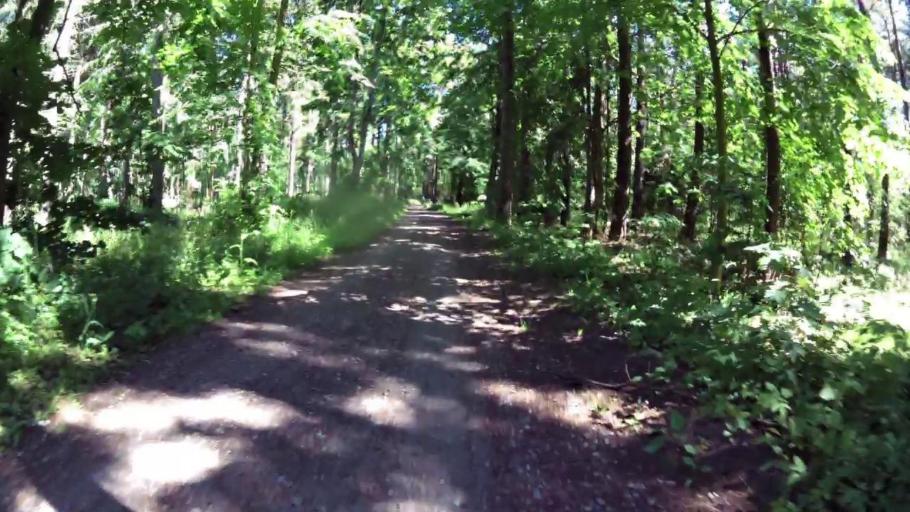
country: PL
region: West Pomeranian Voivodeship
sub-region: Powiat kamienski
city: Dziwnow
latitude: 54.0381
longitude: 14.8257
